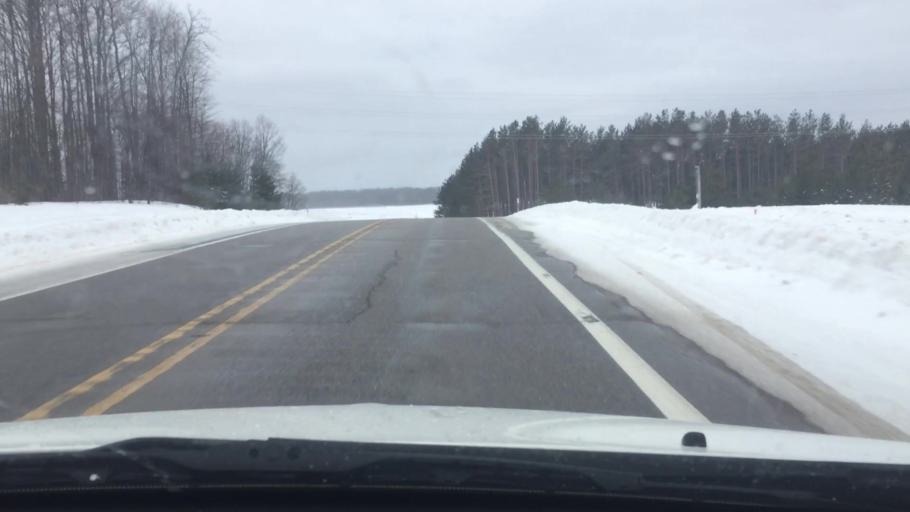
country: US
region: Michigan
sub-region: Charlevoix County
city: Boyne City
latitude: 45.0751
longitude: -84.9020
